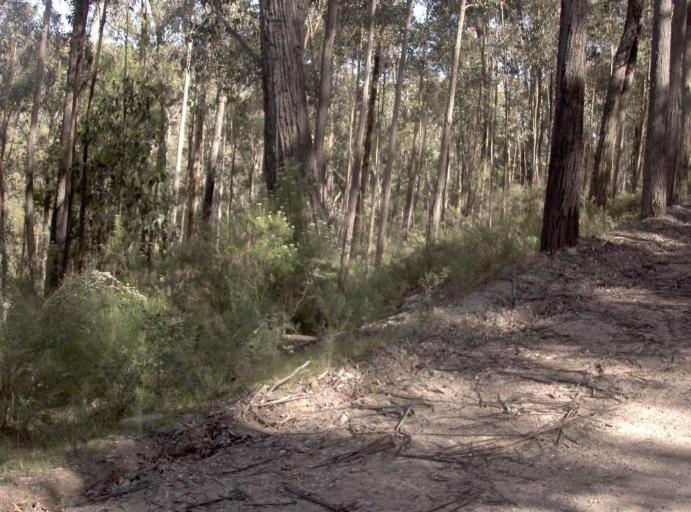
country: AU
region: Victoria
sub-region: East Gippsland
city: Lakes Entrance
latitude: -37.3907
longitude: 148.1254
